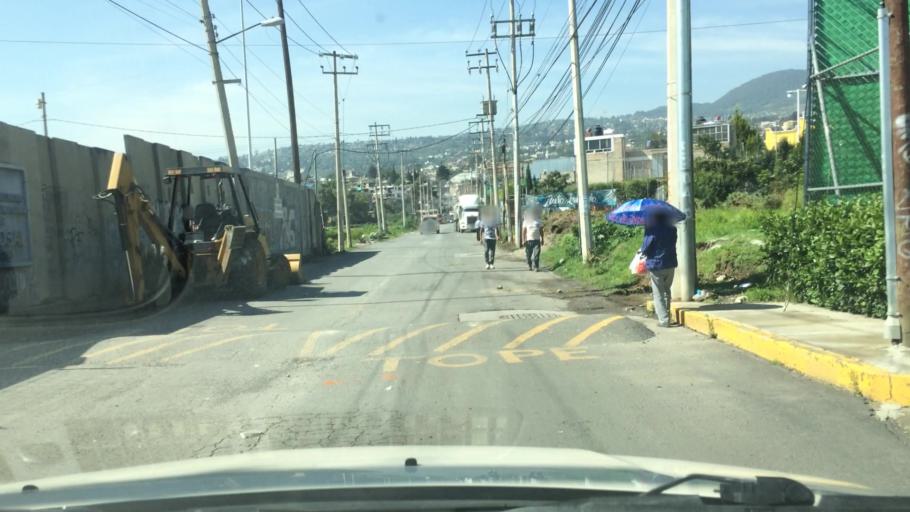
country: MX
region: Mexico City
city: Tlalpan
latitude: 19.2603
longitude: -99.1722
